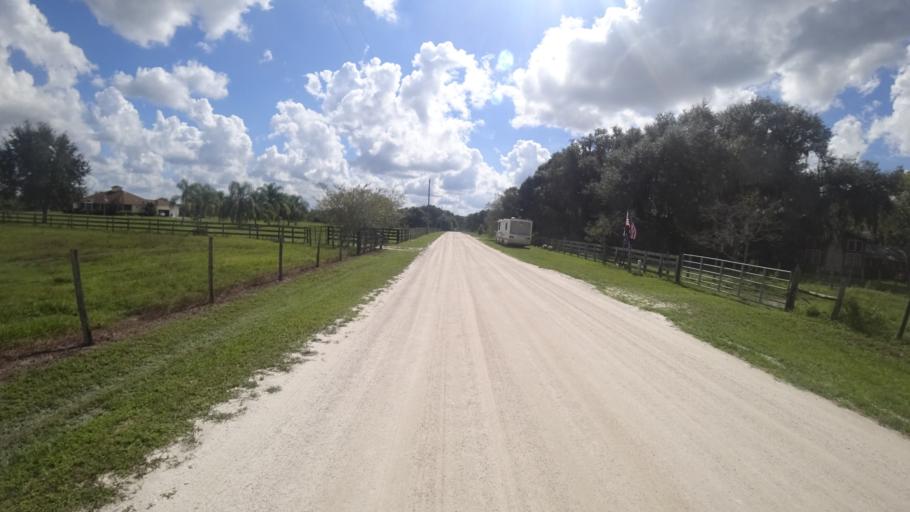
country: US
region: Florida
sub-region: Sarasota County
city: Warm Mineral Springs
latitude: 27.2715
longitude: -82.1543
